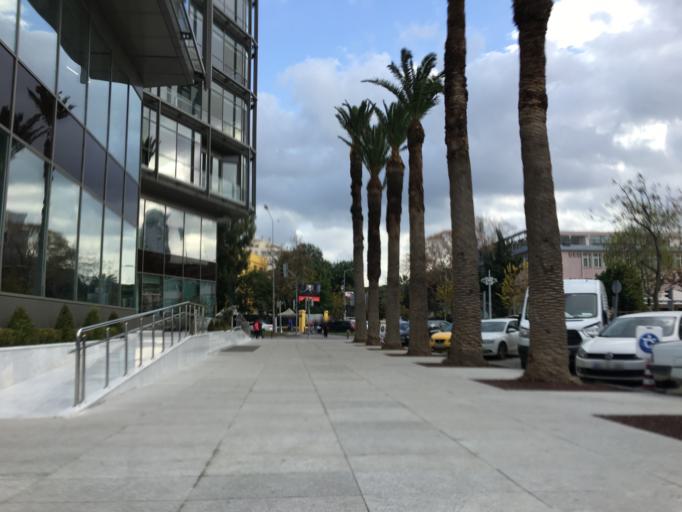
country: TR
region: Izmir
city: Izmir
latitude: 38.4316
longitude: 27.1361
